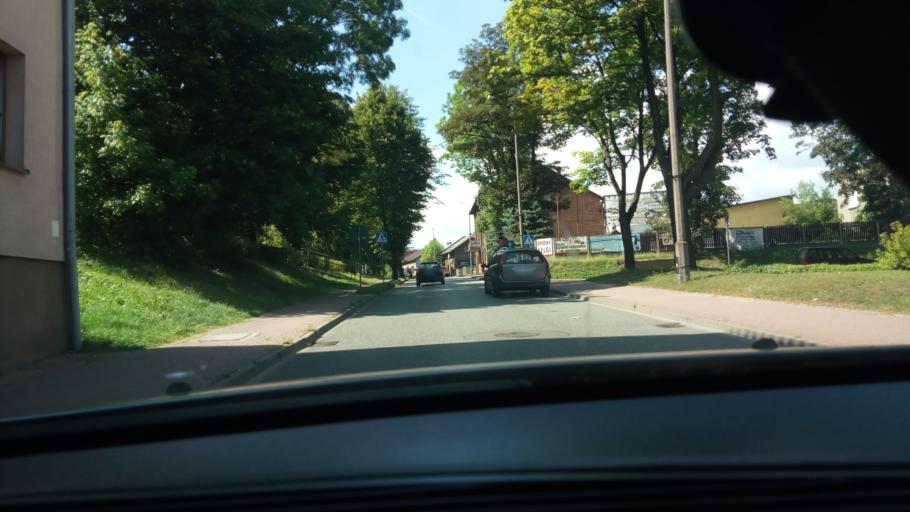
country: PL
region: Lesser Poland Voivodeship
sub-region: Powiat chrzanowski
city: Chrzanow
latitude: 50.1439
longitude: 19.4036
